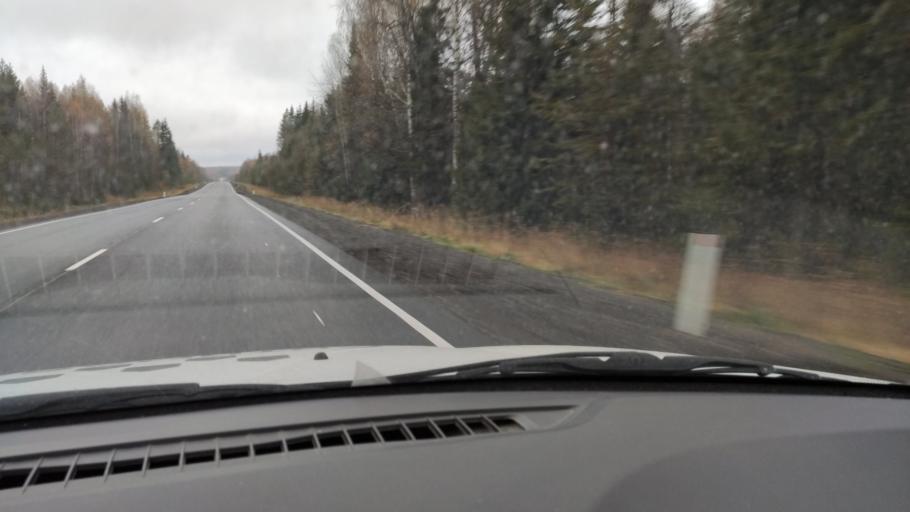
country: RU
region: Kirov
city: Chernaya Kholunitsa
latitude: 58.8867
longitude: 51.3880
